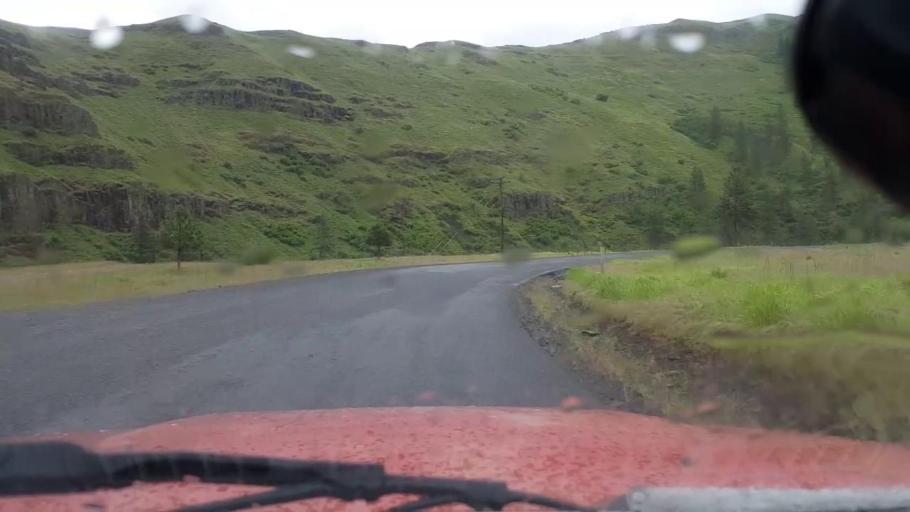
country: US
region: Washington
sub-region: Asotin County
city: Asotin
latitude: 46.0288
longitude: -117.3250
